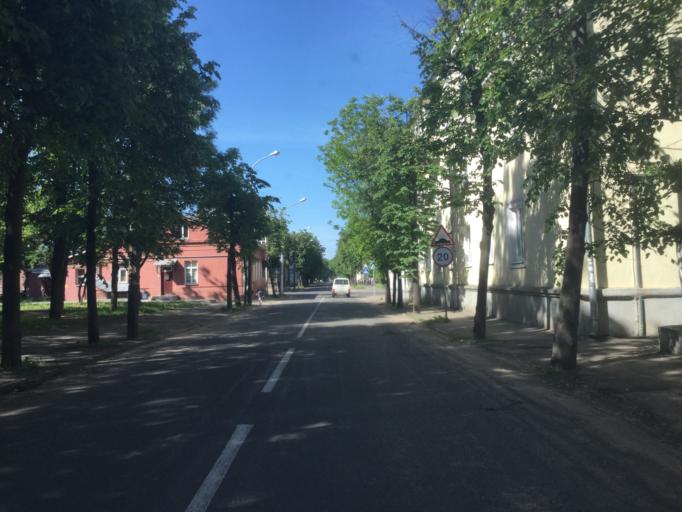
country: BY
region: Vitebsk
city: Vitebsk
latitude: 55.1907
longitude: 30.1911
